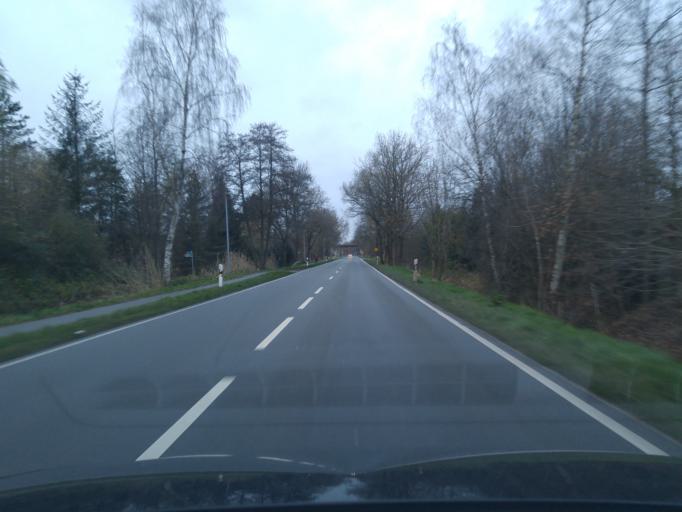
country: DE
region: Schleswig-Holstein
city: Lauenburg
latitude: 53.3610
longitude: 10.5604
